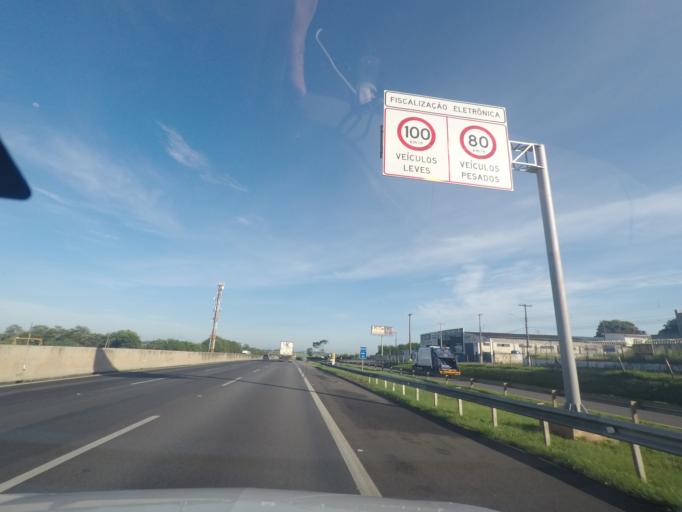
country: BR
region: Sao Paulo
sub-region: Nova Odessa
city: Nova Odessa
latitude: -22.7507
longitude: -47.2609
